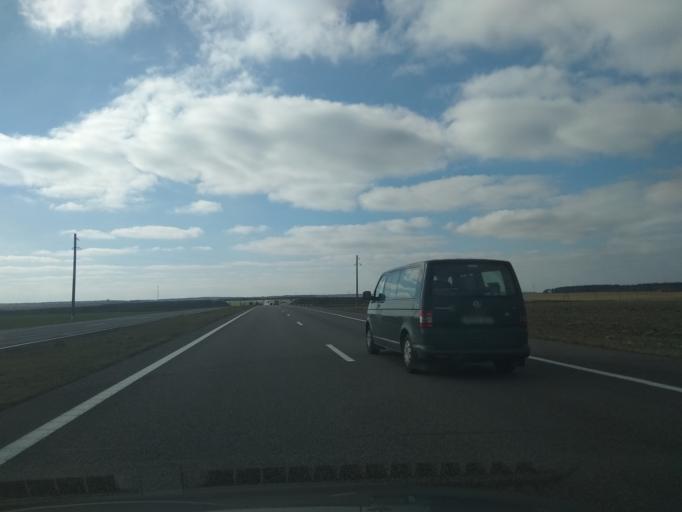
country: BY
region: Minsk
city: Haradzyeya
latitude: 53.4094
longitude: 26.5613
